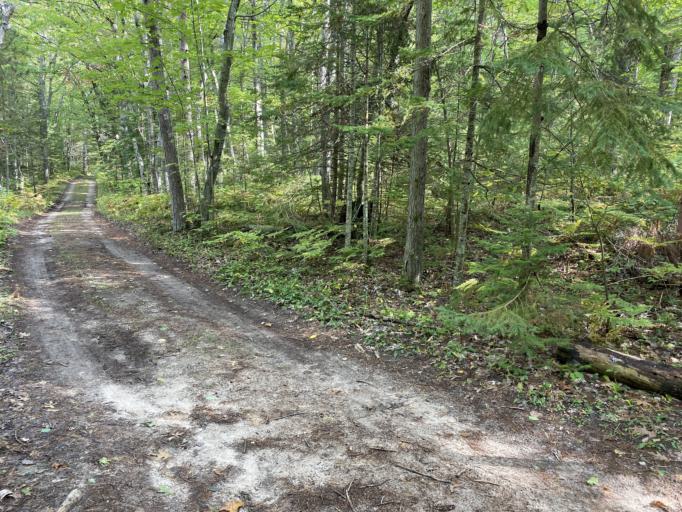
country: US
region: Michigan
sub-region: Mackinac County
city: Saint Ignace
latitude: 45.7453
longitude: -84.8789
